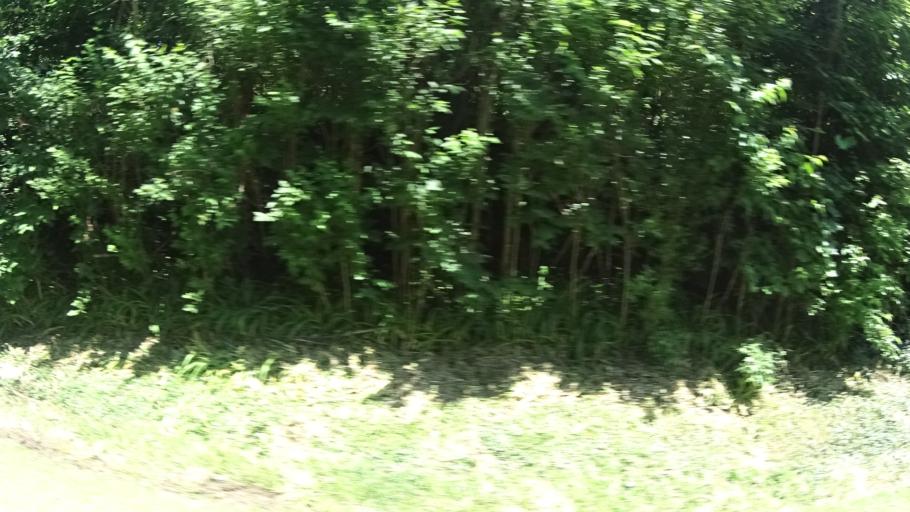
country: US
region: Ohio
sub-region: Lorain County
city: Vermilion
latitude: 41.3492
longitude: -82.4246
